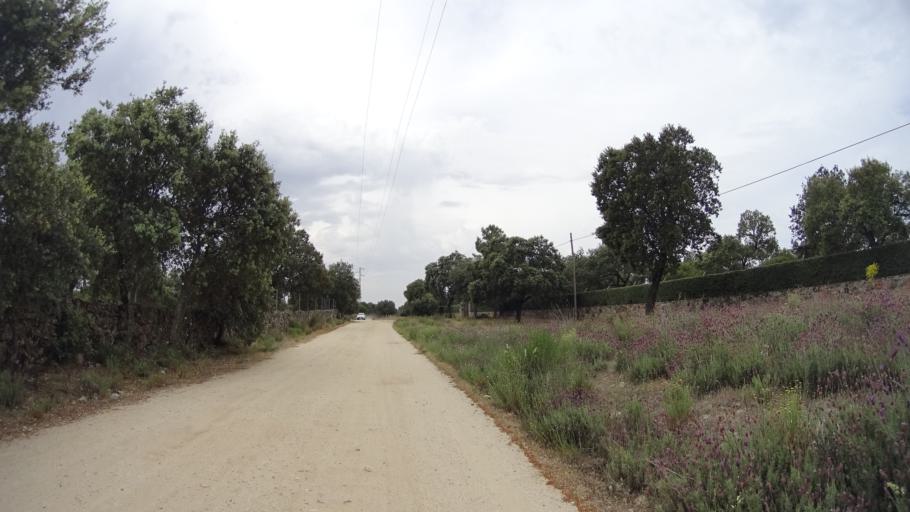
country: ES
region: Madrid
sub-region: Provincia de Madrid
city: Colmenarejo
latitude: 40.5533
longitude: -4.0374
